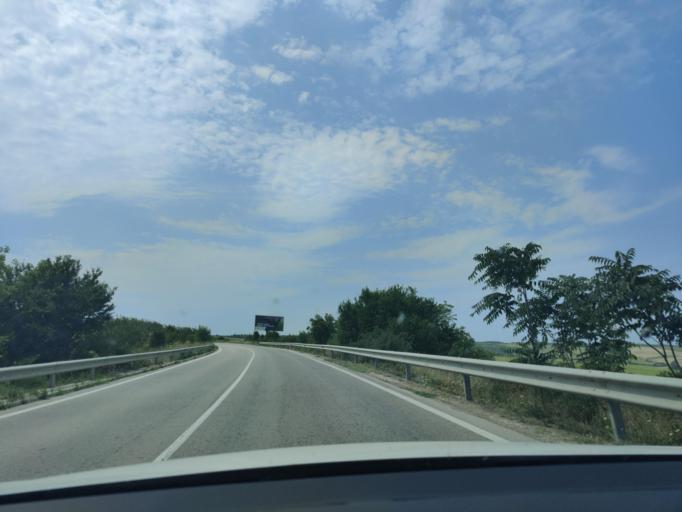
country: BG
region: Vidin
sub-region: Obshtina Vidin
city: Dunavtsi
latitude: 43.8939
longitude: 22.7948
